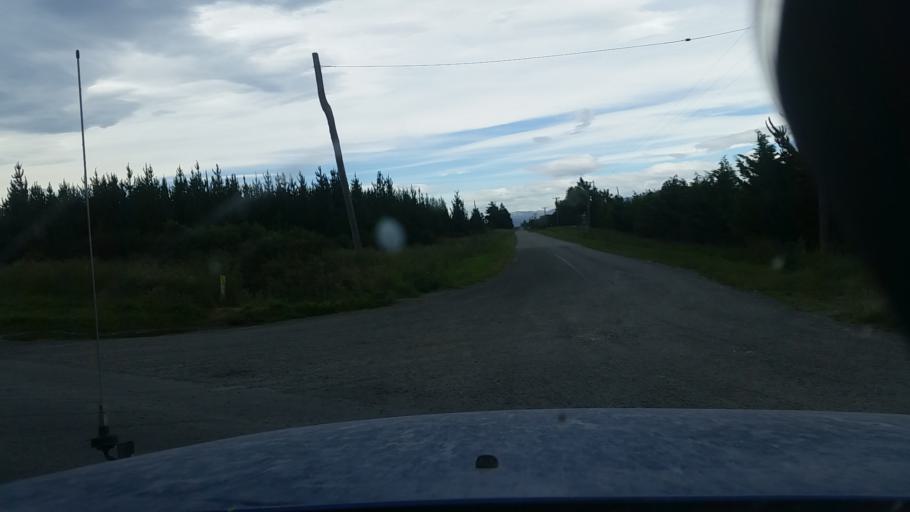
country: NZ
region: Canterbury
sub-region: Ashburton District
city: Methven
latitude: -43.7853
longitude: 171.5358
